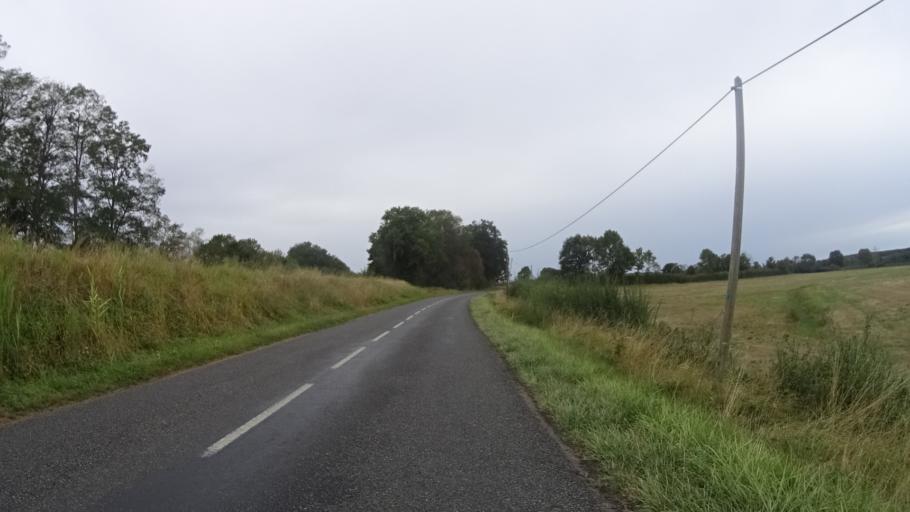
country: FR
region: Bourgogne
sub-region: Departement de la Nievre
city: Decize
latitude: 46.7905
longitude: 3.5130
